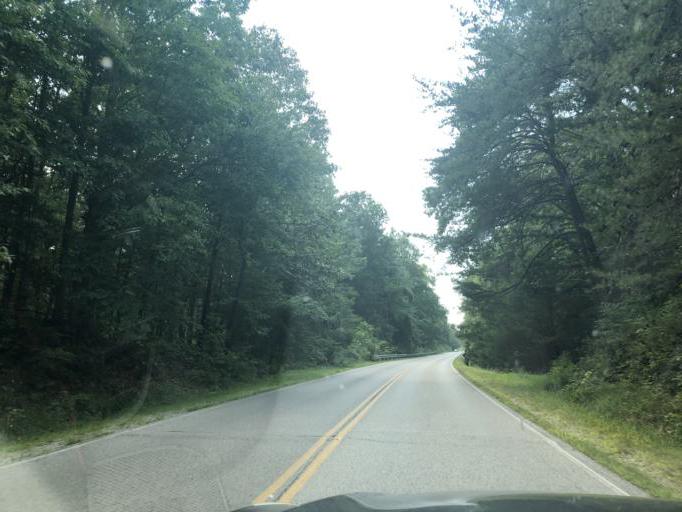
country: US
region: Tennessee
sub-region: Franklin County
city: Sewanee
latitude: 35.2075
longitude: -85.9061
